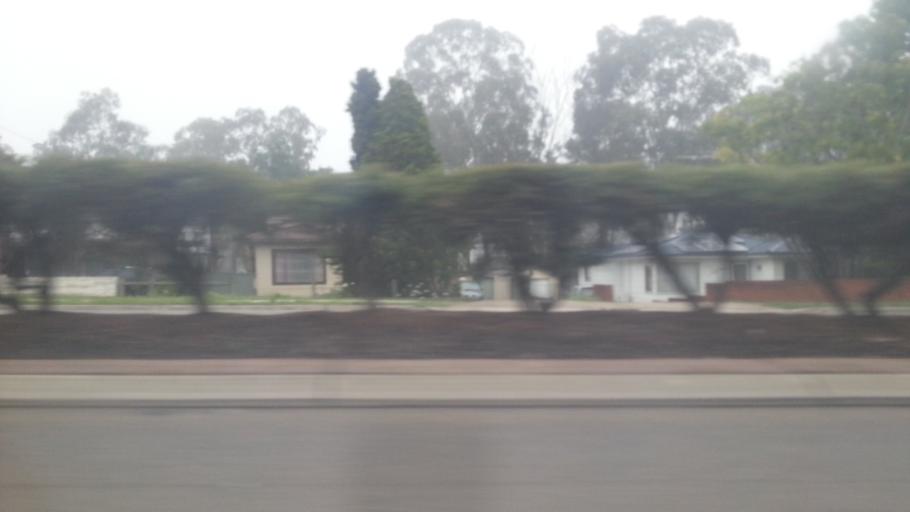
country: AU
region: New South Wales
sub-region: Penrith Municipality
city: Cambridge Park
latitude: -33.7452
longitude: 150.7147
